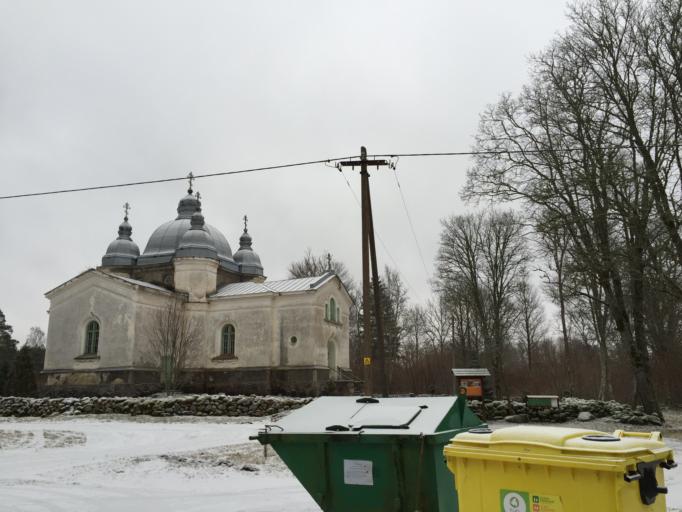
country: EE
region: Saare
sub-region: Orissaare vald
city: Orissaare
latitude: 58.6193
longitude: 23.1844
